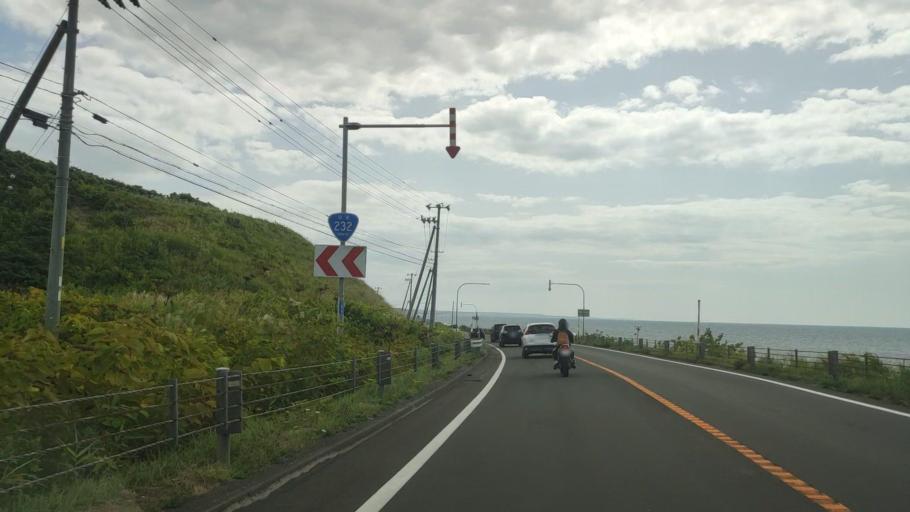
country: JP
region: Hokkaido
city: Rumoi
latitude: 44.5095
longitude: 141.7650
